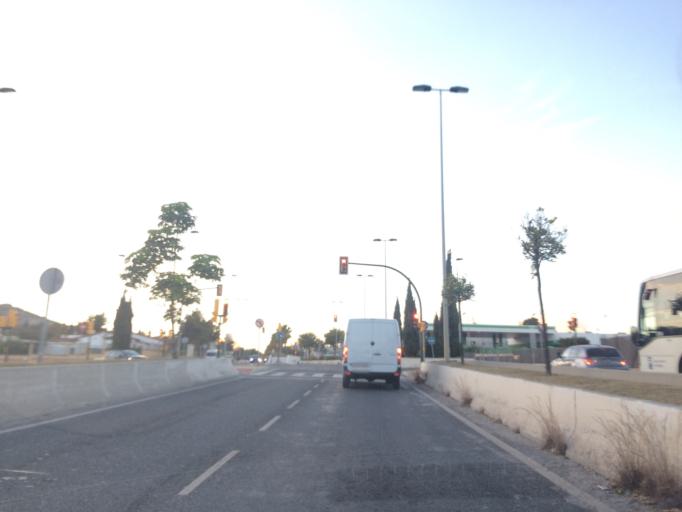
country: ES
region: Andalusia
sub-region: Provincia de Malaga
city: Torremolinos
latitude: 36.6591
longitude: -4.4917
